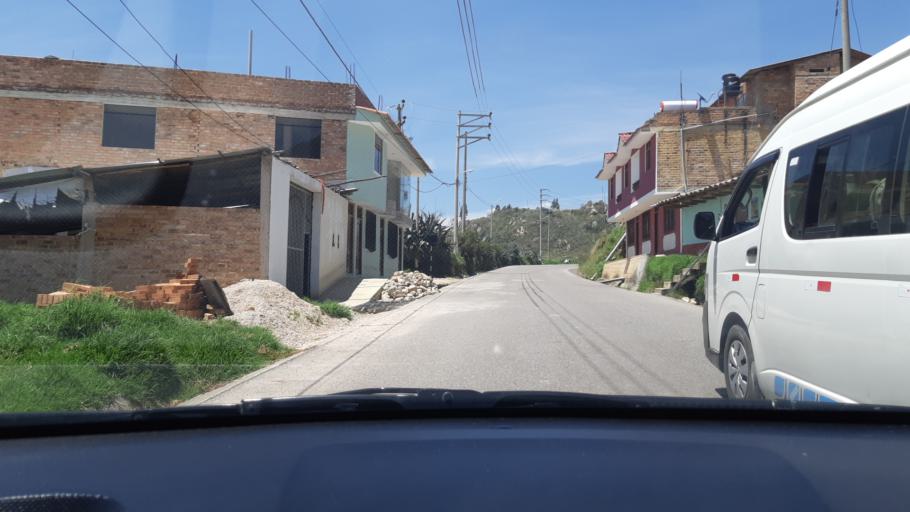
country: PE
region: Cajamarca
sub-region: Provincia de Cajamarca
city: Llacanora
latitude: -7.1759
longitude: -78.4575
